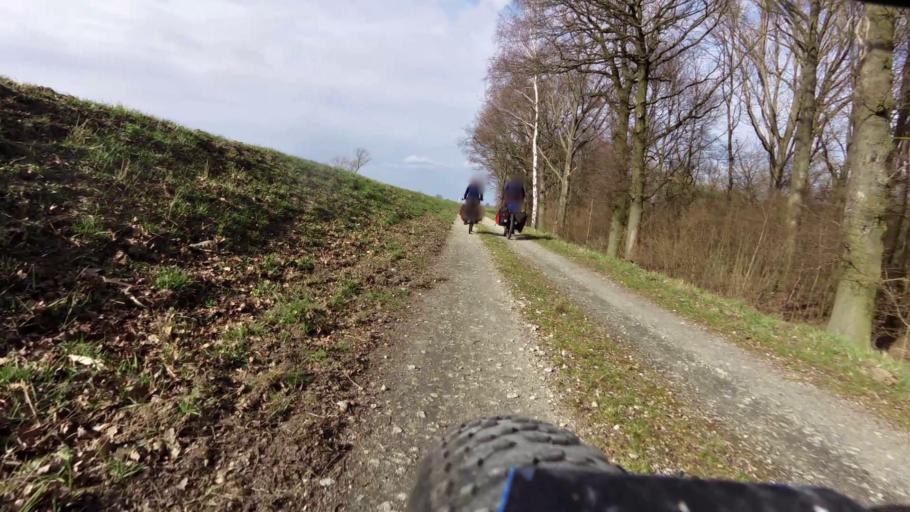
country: DE
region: Brandenburg
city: Reitwein
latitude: 52.5235
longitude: 14.6106
